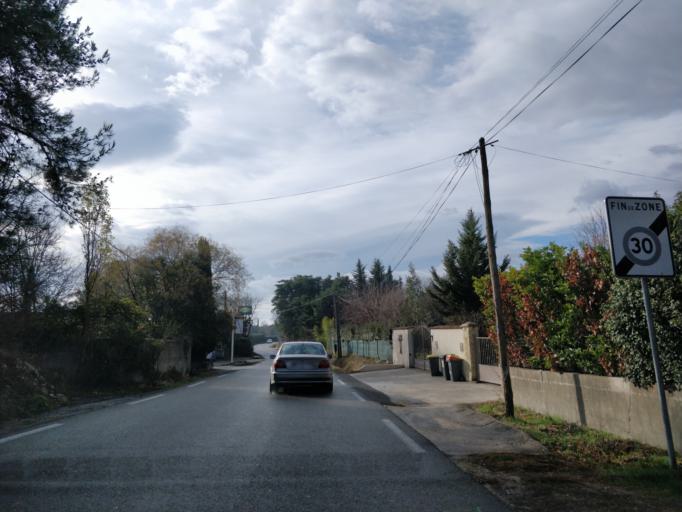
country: FR
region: Languedoc-Roussillon
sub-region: Departement du Gard
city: Villevieille
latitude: 43.8111
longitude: 4.1210
